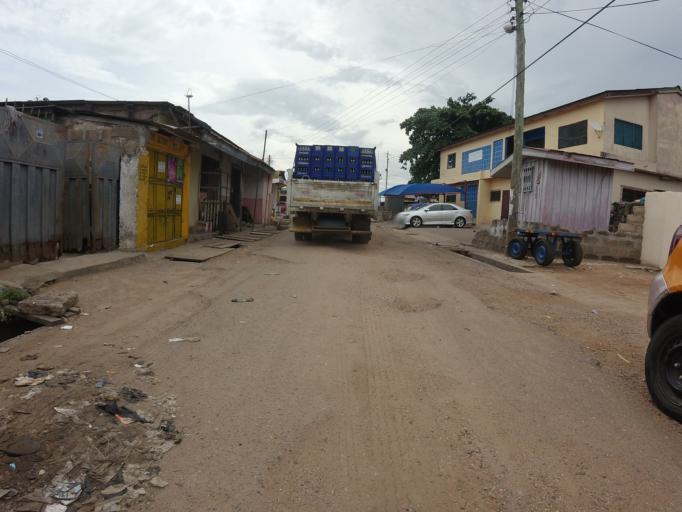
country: GH
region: Greater Accra
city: Accra
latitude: 5.5973
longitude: -0.2166
